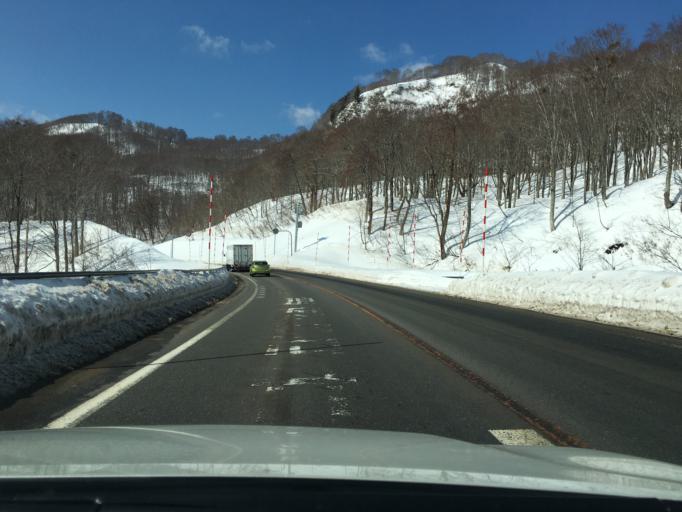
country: JP
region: Yamagata
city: Tsuruoka
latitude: 38.5322
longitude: 139.9497
